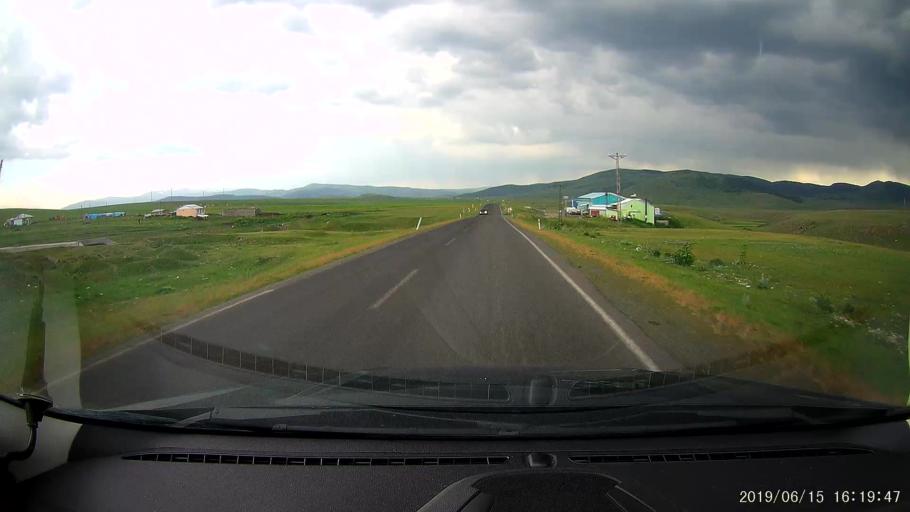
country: TR
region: Ardahan
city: Hanak
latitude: 41.2248
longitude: 42.8500
